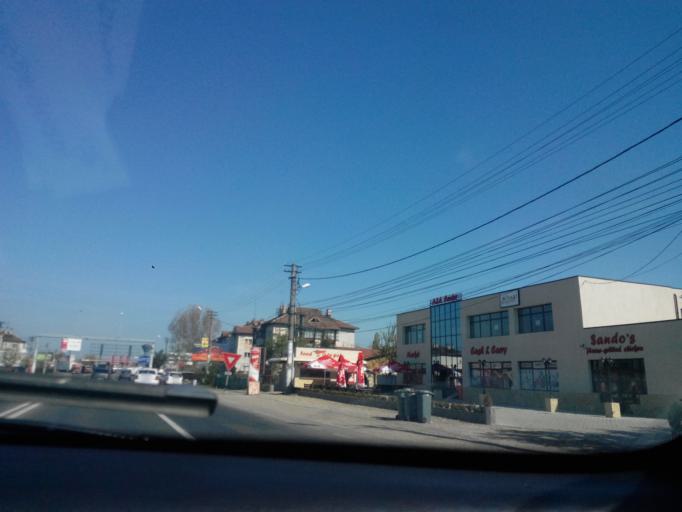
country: RO
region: Prahova
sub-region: Comuna Barcanesti
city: Barcanesti
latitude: 44.8831
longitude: 26.0482
